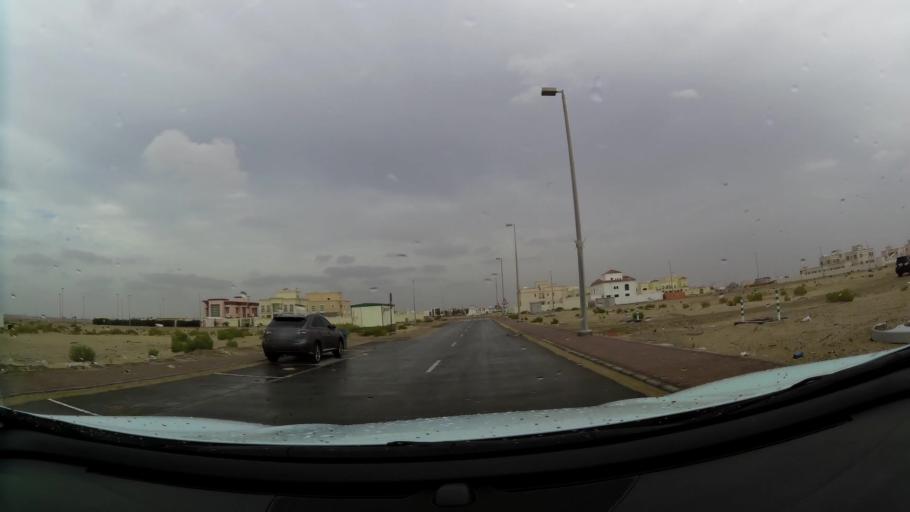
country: AE
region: Abu Dhabi
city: Abu Dhabi
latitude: 24.3654
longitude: 54.6223
